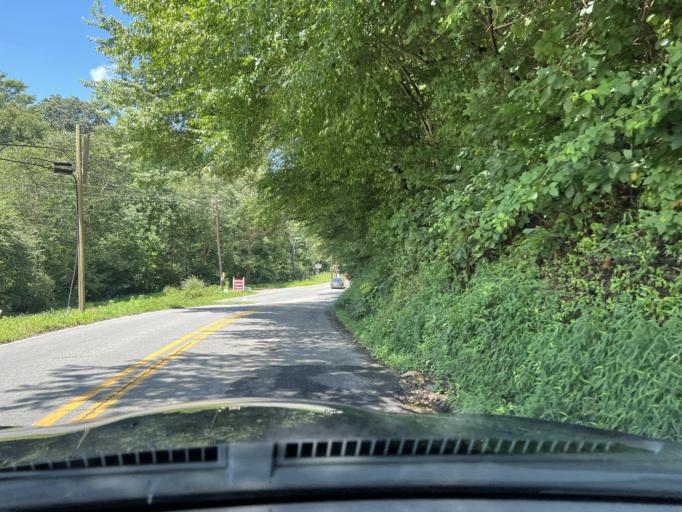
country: US
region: North Carolina
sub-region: Buncombe County
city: Fairview
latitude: 35.5167
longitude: -82.4001
